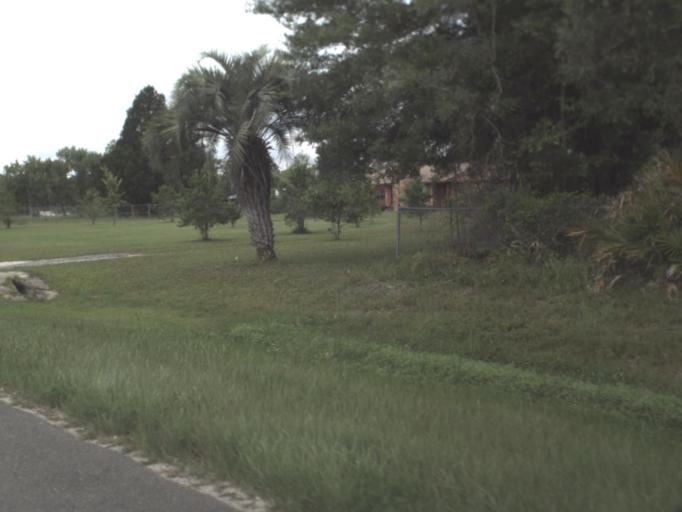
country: US
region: Florida
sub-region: Clay County
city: Keystone Heights
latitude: 29.8205
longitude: -82.0604
